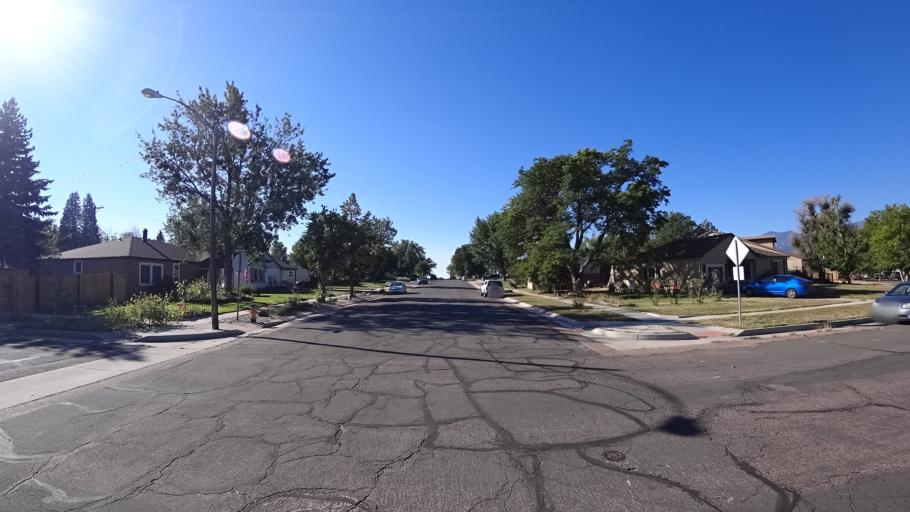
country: US
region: Colorado
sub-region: El Paso County
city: Colorado Springs
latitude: 38.8660
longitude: -104.7974
